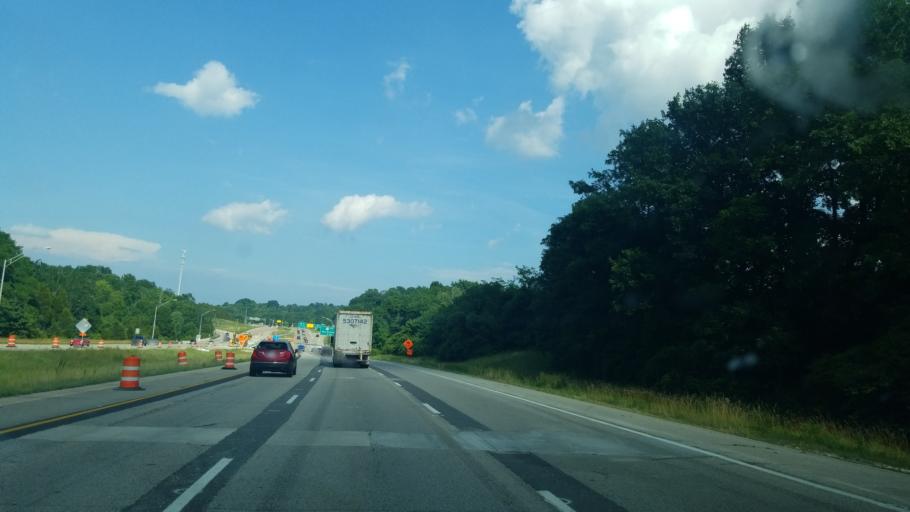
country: US
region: Kentucky
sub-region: Campbell County
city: Silver Grove
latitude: 39.0553
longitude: -84.4039
